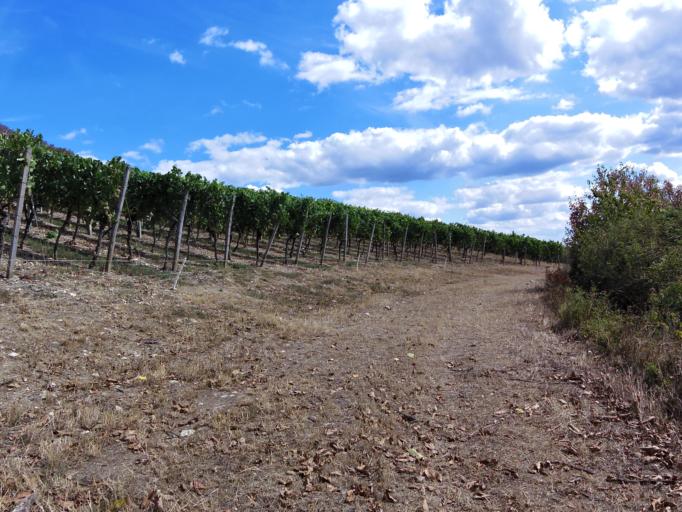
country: DE
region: Bavaria
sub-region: Regierungsbezirk Unterfranken
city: Margetshochheim
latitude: 49.8545
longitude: 9.8626
